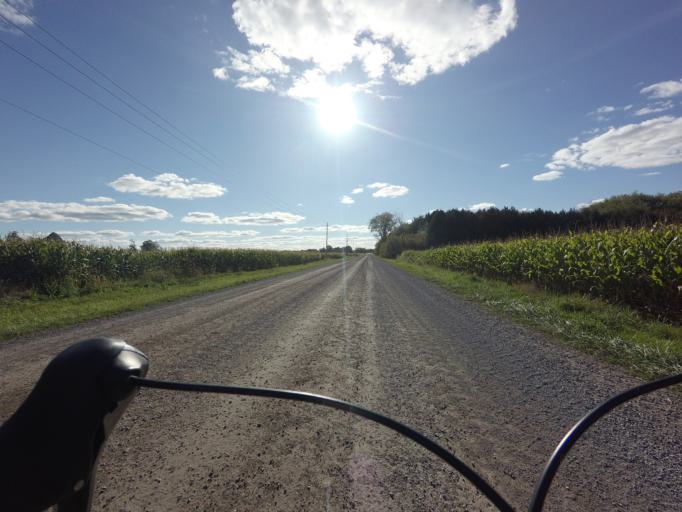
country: CA
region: Ontario
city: Bells Corners
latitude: 45.1101
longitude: -75.7180
